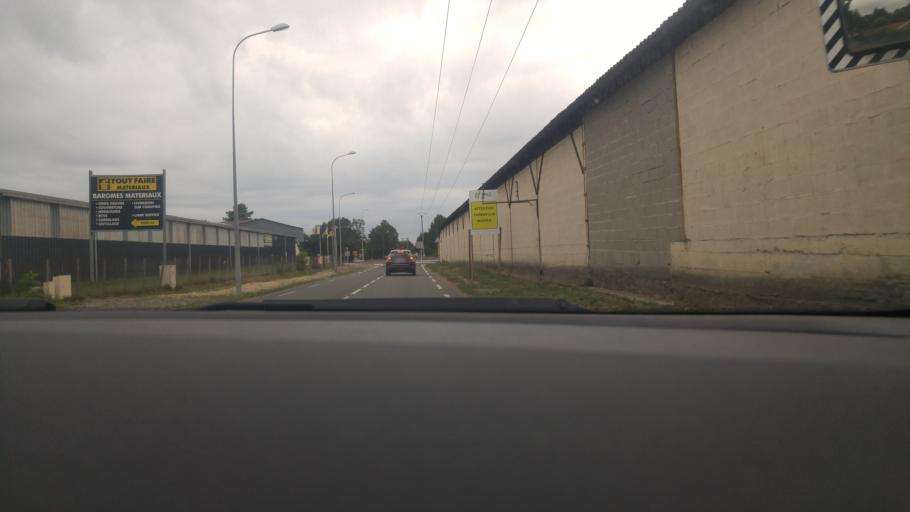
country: FR
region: Aquitaine
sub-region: Departement des Landes
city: Soustons
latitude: 43.7472
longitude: -1.3244
